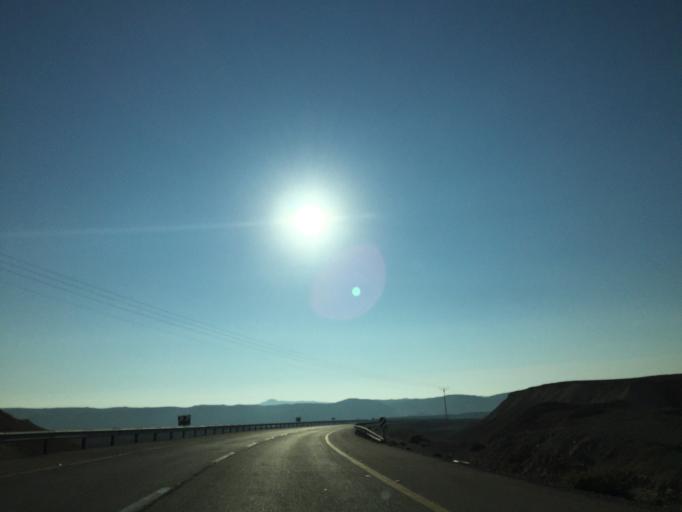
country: IL
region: Southern District
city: Mitzpe Ramon
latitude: 30.2886
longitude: 34.9968
